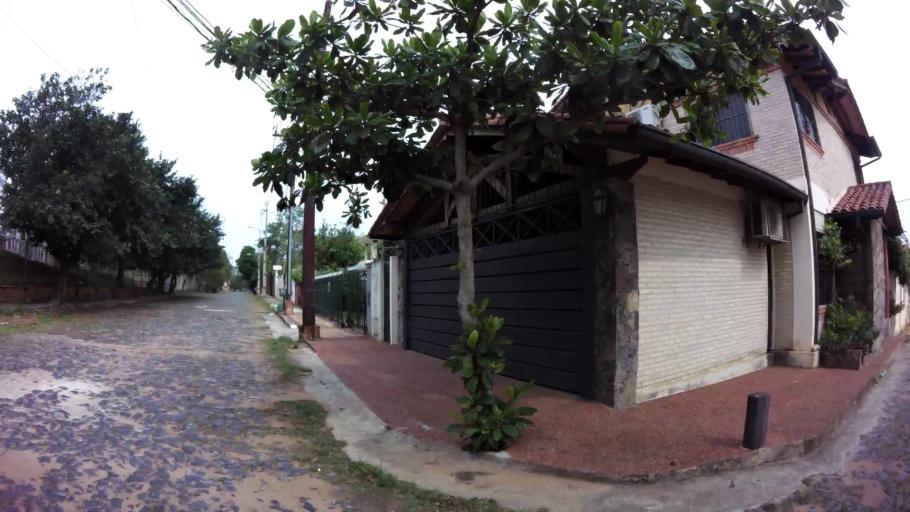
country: PY
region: Central
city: Lambare
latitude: -25.2954
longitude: -57.5691
